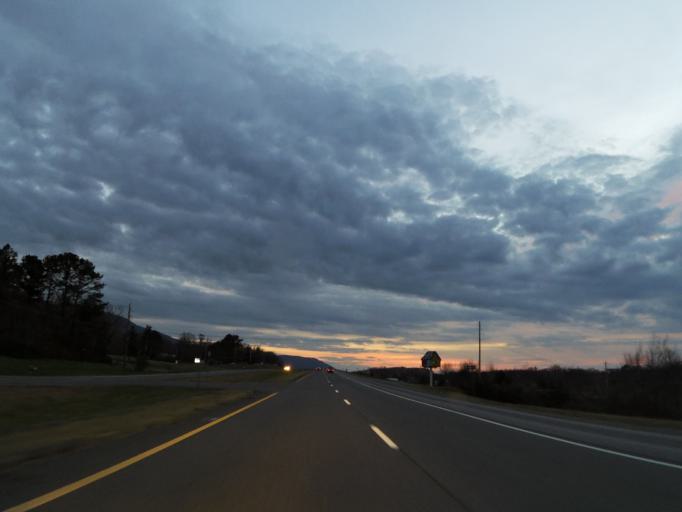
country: US
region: Tennessee
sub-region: McMinn County
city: Etowah
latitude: 35.2519
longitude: -84.5563
